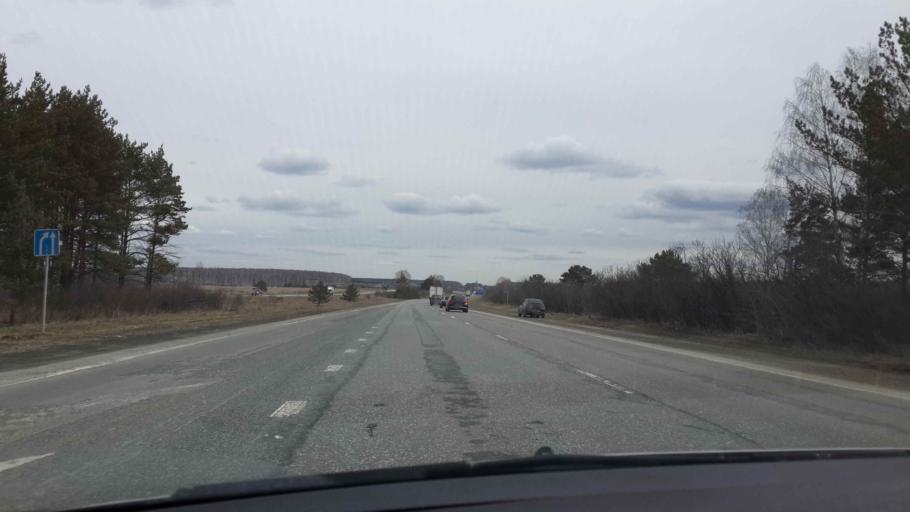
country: RU
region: Sverdlovsk
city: Verkhneye Dubrovo
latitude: 56.7341
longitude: 61.0827
